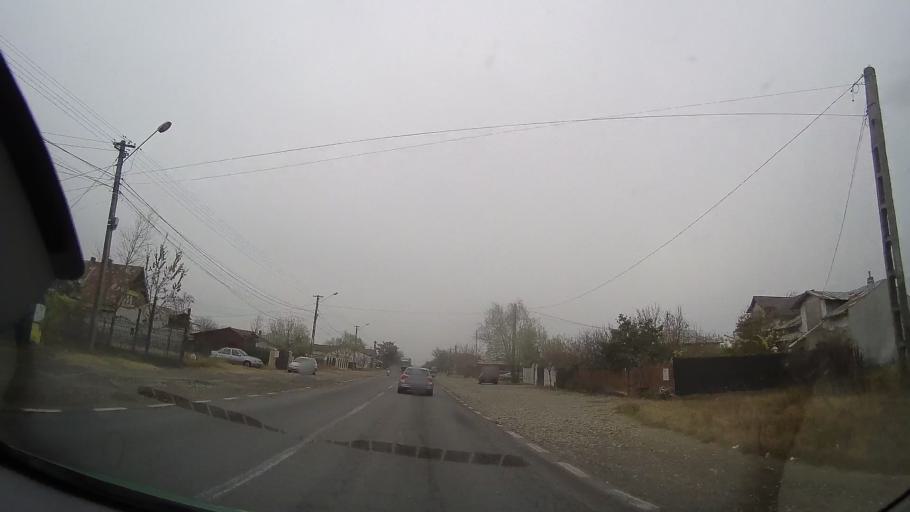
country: RO
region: Prahova
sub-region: Comuna Blejoiu
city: Ploiestiori
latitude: 44.9717
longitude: 26.0222
